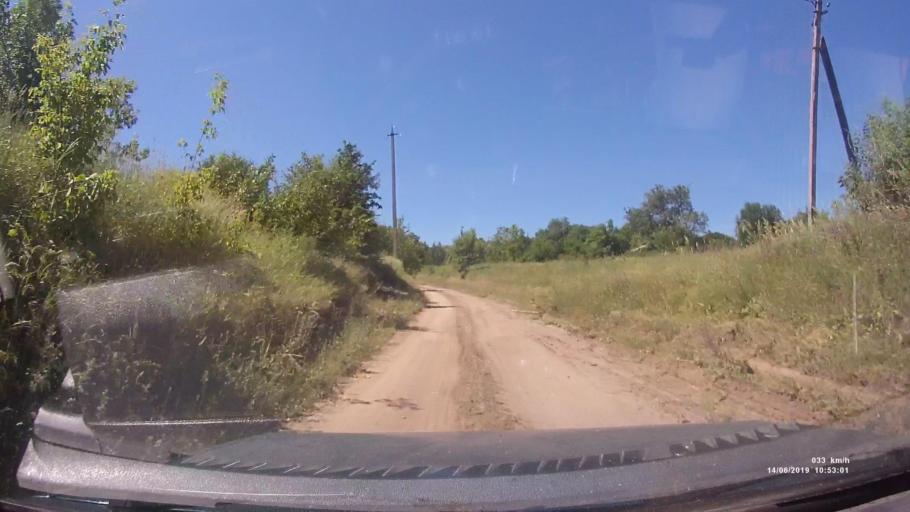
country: RU
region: Rostov
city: Kazanskaya
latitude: 49.8644
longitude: 41.3834
